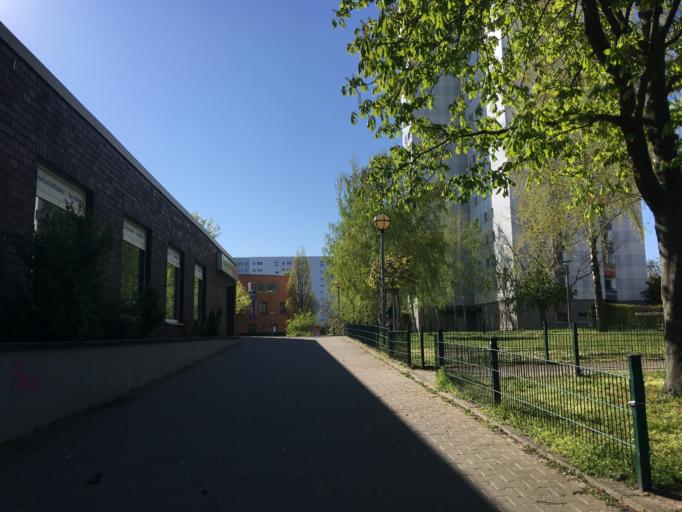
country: DE
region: Berlin
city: Neu-Hohenschoenhausen
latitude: 52.5686
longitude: 13.5148
